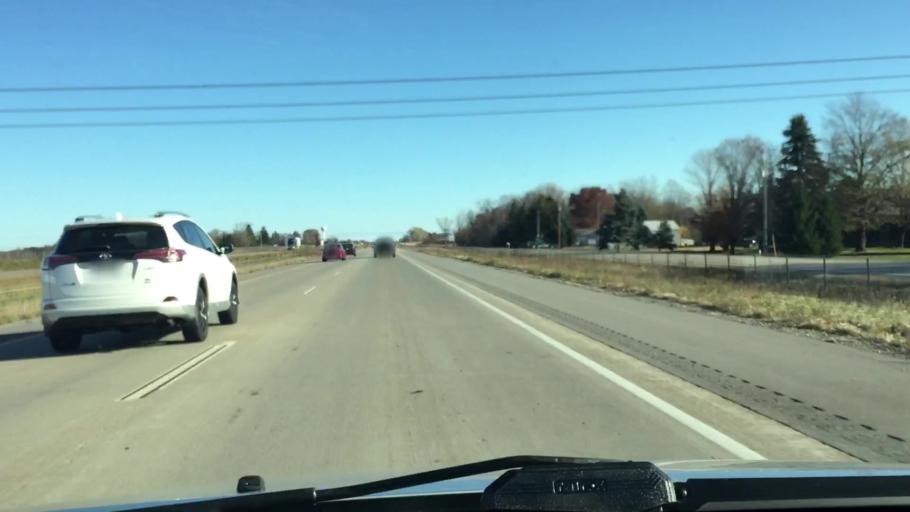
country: US
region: Wisconsin
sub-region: Brown County
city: Wrightstown
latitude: 44.3989
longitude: -88.1516
